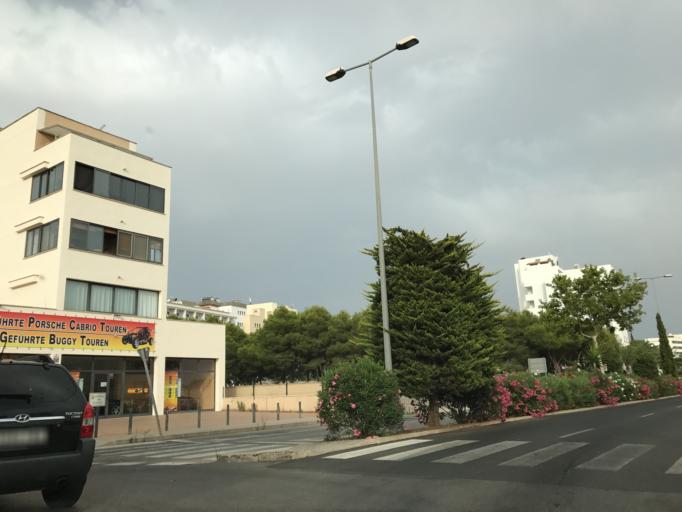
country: ES
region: Balearic Islands
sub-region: Illes Balears
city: Son Servera
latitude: 39.5958
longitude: 3.3794
